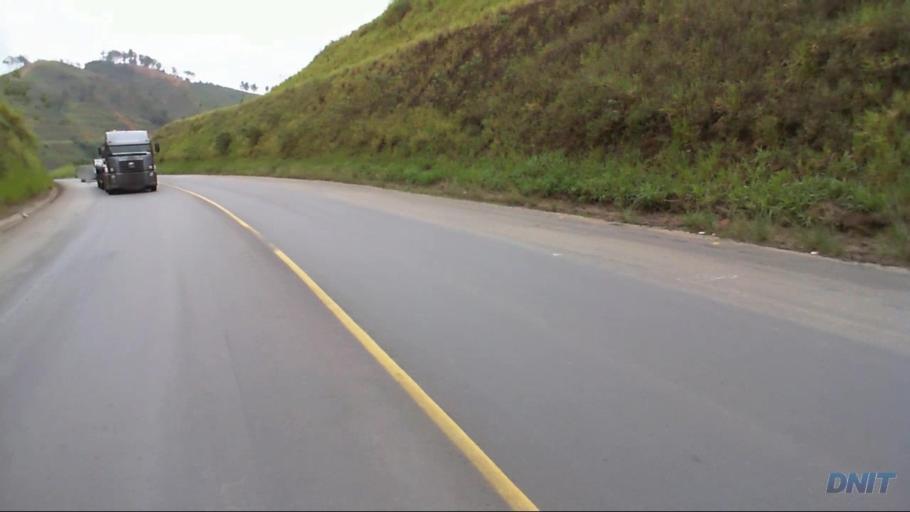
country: BR
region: Minas Gerais
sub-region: Coronel Fabriciano
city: Coronel Fabriciano
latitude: -19.5351
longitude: -42.6729
